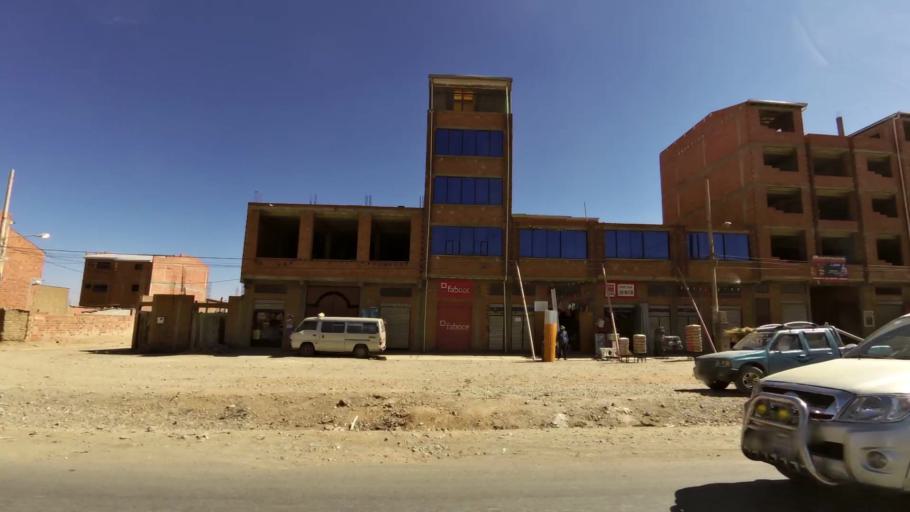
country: BO
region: La Paz
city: La Paz
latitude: -16.5438
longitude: -68.1993
